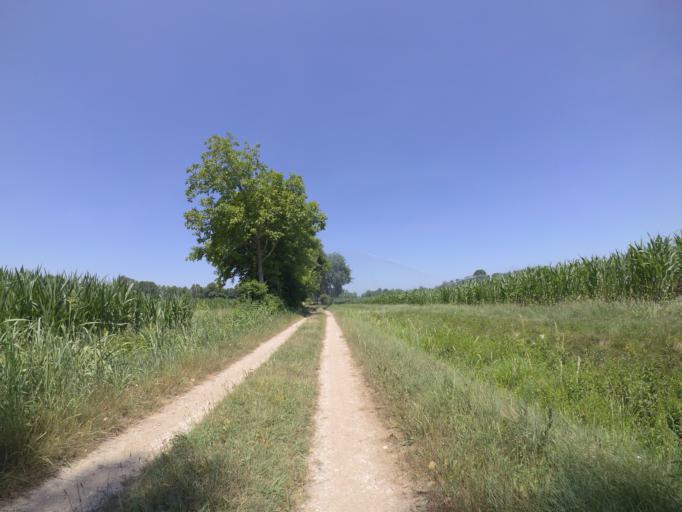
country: IT
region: Friuli Venezia Giulia
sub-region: Provincia di Udine
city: Talmassons
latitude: 45.9196
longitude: 13.0929
